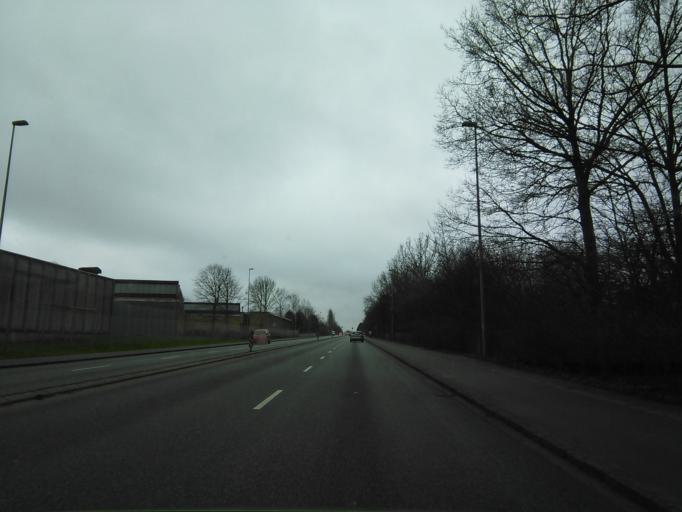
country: DK
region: Central Jutland
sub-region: Arhus Kommune
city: Stavtrup
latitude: 56.1109
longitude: 10.1545
